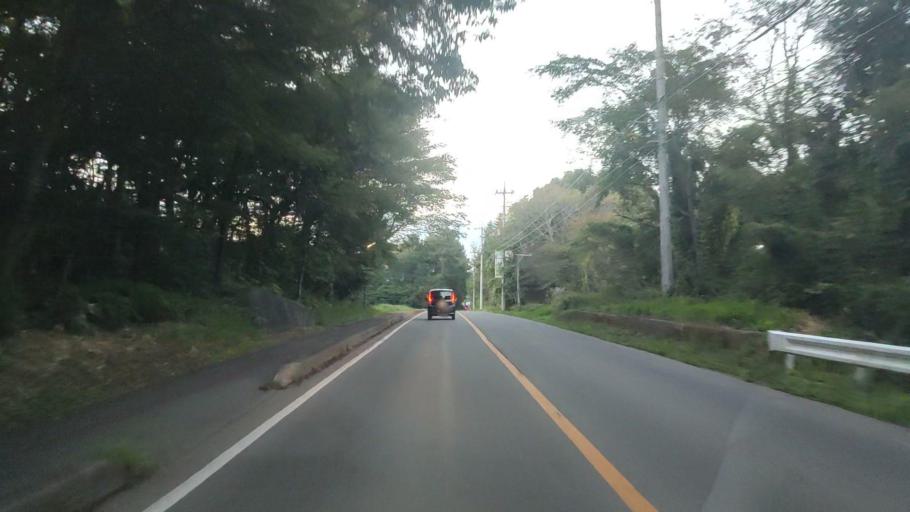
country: JP
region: Nagano
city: Komoro
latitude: 36.4930
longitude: 138.5844
